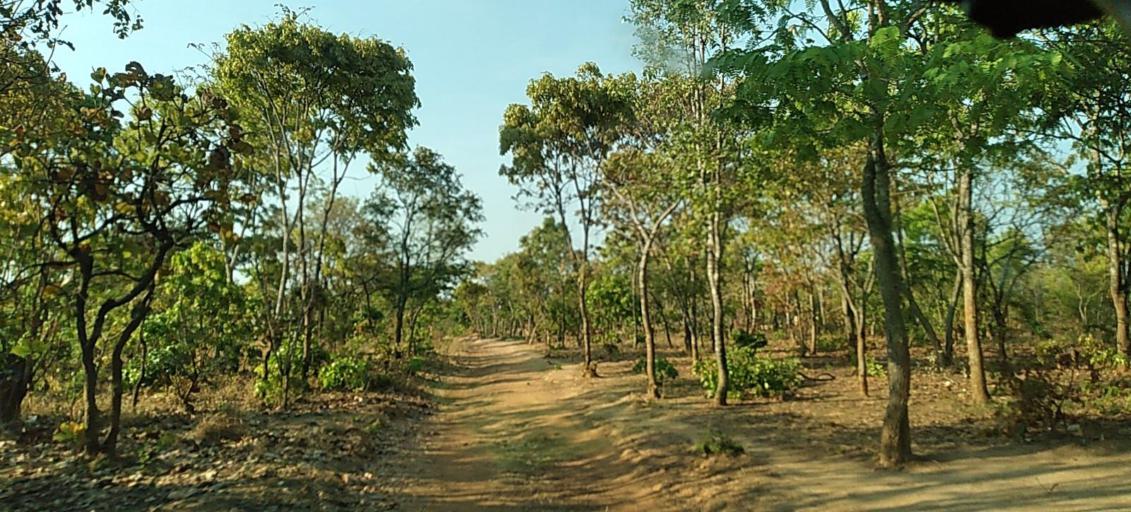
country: ZM
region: North-Western
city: Kalengwa
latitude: -13.1544
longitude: 25.0339
